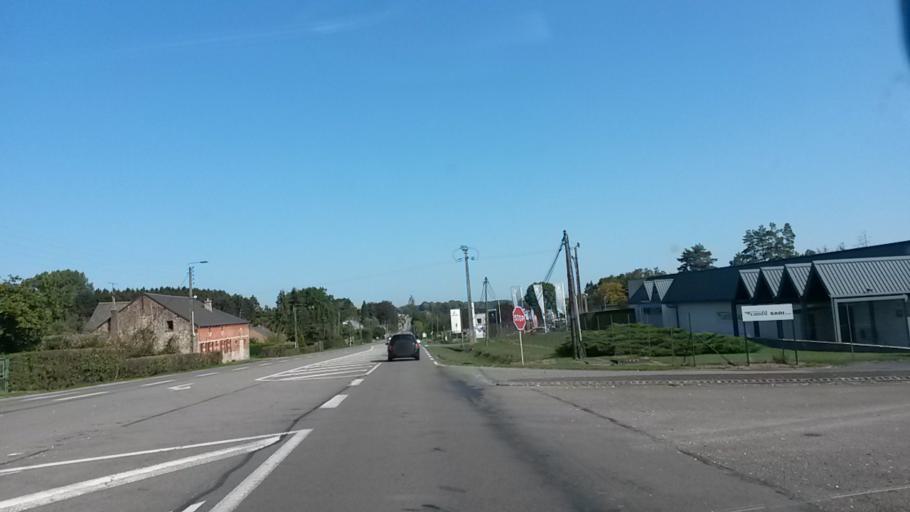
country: FR
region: Nord-Pas-de-Calais
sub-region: Departement du Nord
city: Avesnes-sur-Helpe
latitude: 50.1071
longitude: 3.9316
